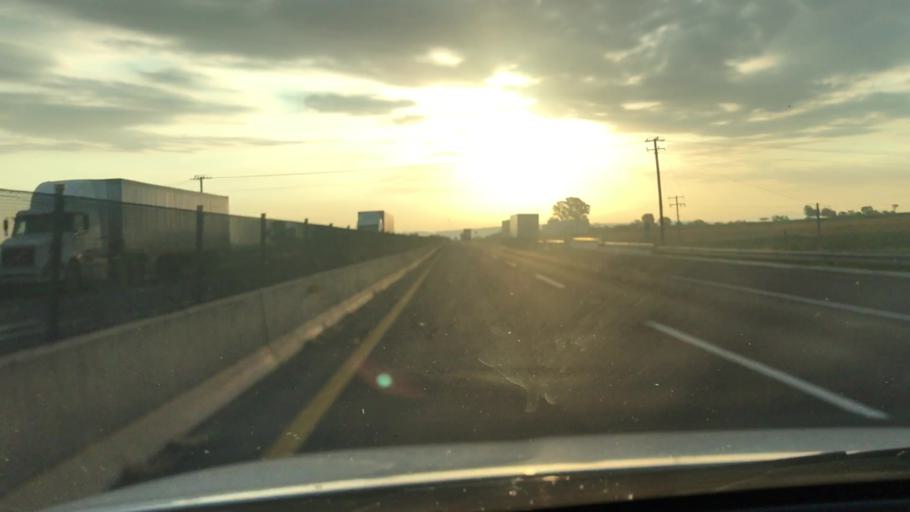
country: MX
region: Jalisco
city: Acatic
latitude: 20.7378
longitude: -102.9110
